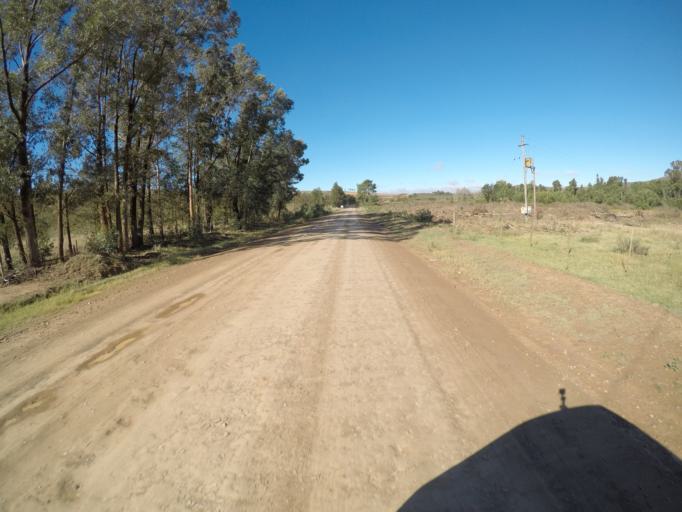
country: ZA
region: Western Cape
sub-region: Overberg District Municipality
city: Caledon
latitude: -34.0740
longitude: 19.6402
